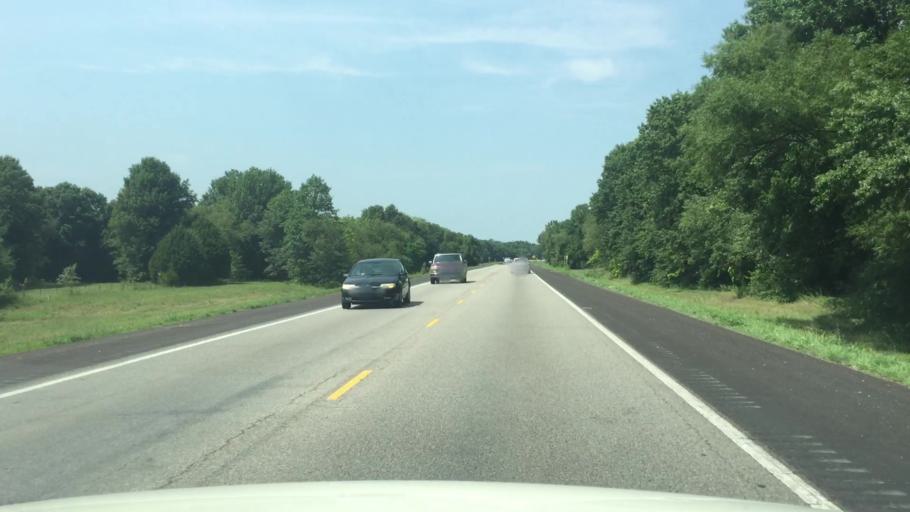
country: US
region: Kansas
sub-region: Crawford County
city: Pittsburg
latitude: 37.4004
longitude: -94.7211
